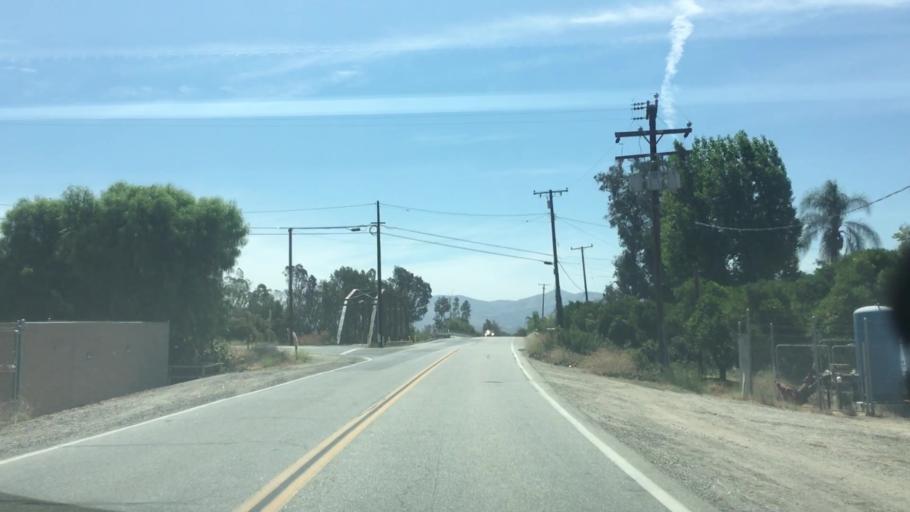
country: US
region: California
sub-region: Ventura County
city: Fillmore
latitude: 34.4079
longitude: -118.9356
